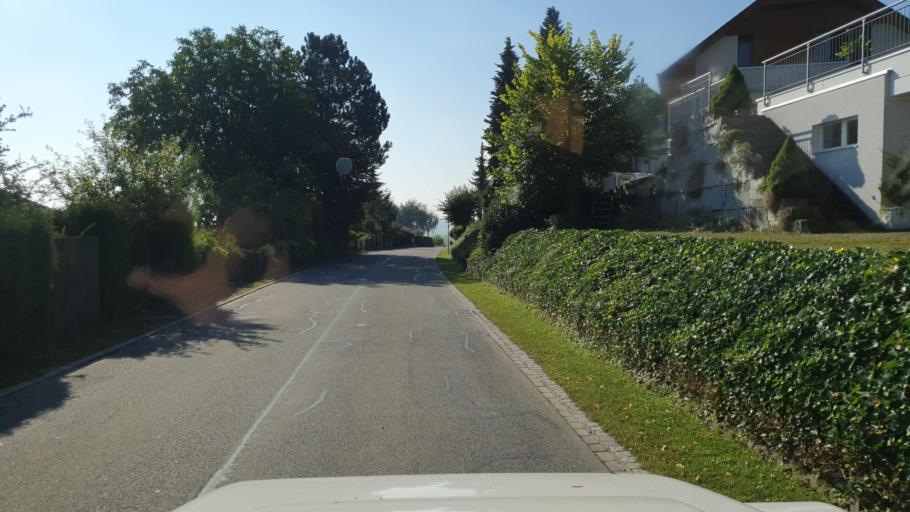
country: CH
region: Aargau
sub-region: Bezirk Muri
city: Waltenschwil
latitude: 47.3119
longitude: 8.2944
